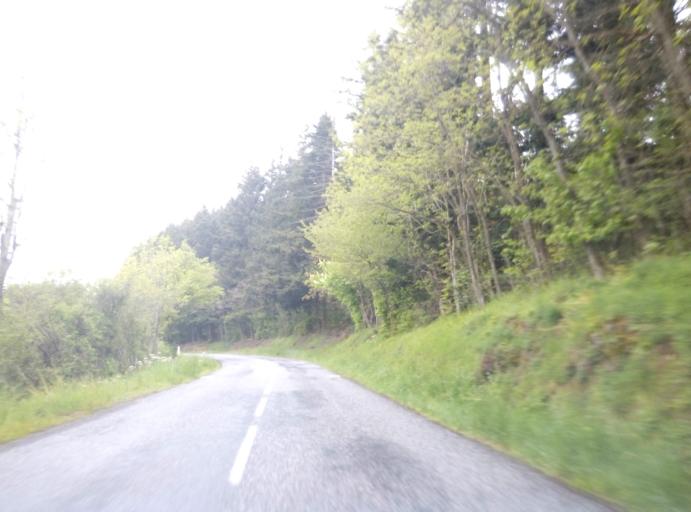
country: FR
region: Rhone-Alpes
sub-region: Departement du Rhone
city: Tarare
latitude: 45.9276
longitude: 4.4282
